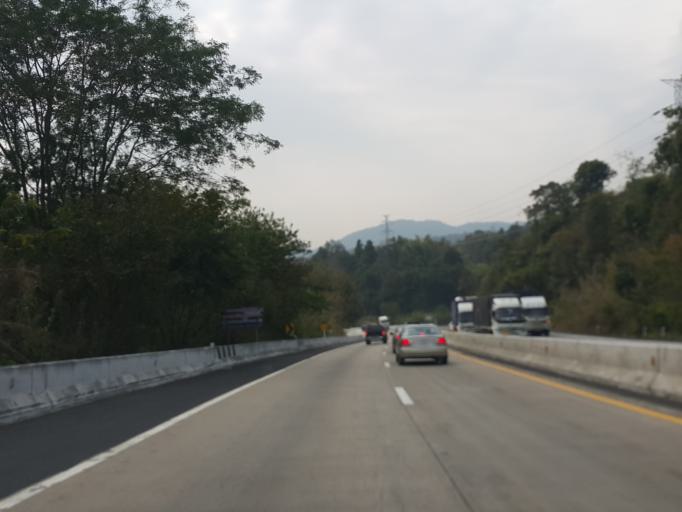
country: TH
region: Lamphun
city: Mae Tha
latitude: 18.4187
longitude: 99.2094
